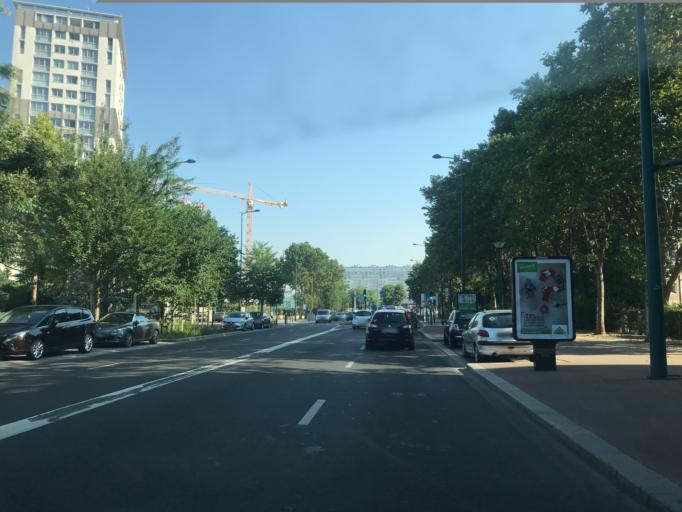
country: FR
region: Ile-de-France
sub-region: Departement des Hauts-de-Seine
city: Asnieres-sur-Seine
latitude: 48.9285
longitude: 2.2845
